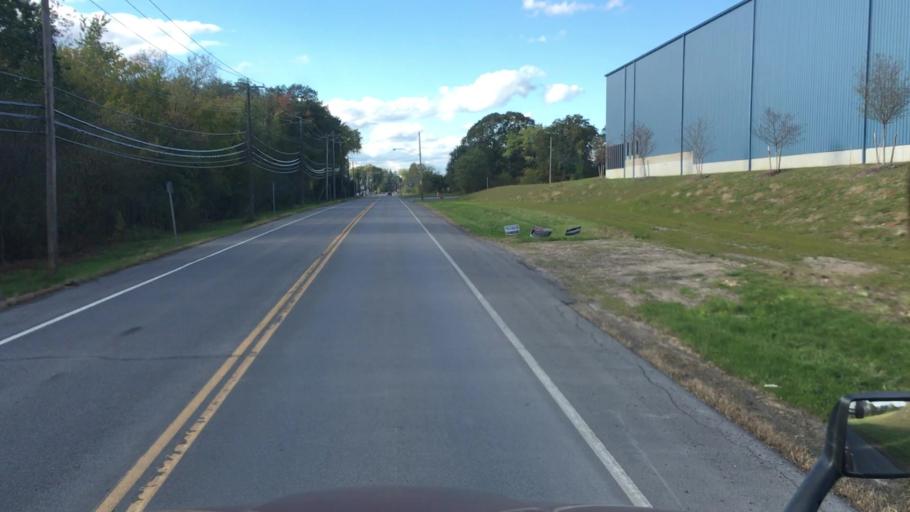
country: US
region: New York
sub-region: Schenectady County
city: Scotia
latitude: 42.8346
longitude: -73.9855
